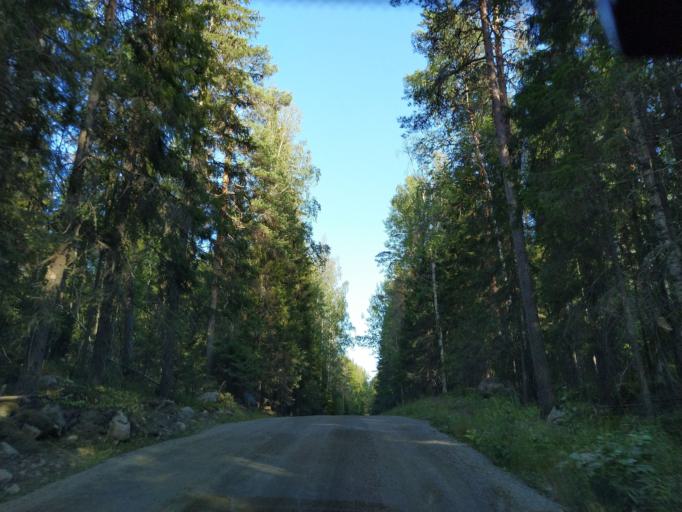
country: FI
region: Central Finland
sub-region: Jaemsae
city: Kuhmoinen
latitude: 61.6786
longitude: 24.9876
